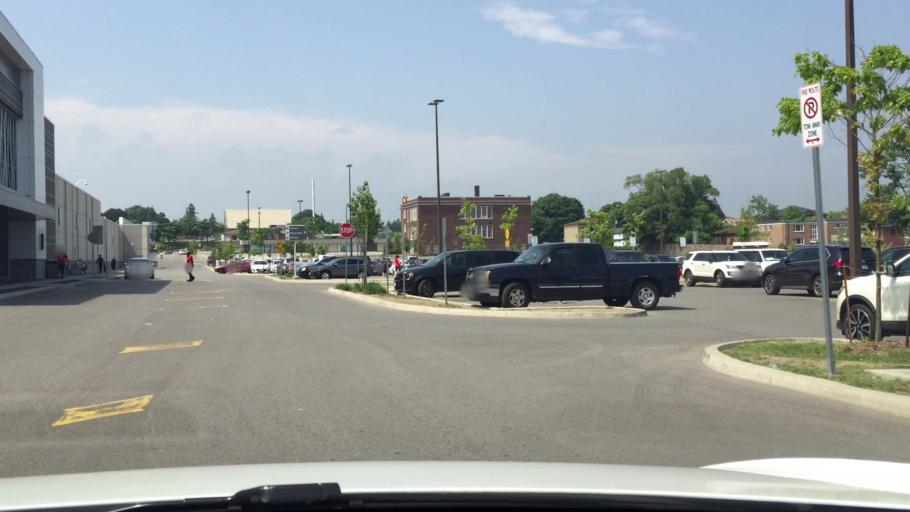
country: CA
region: Ontario
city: Oshawa
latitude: 43.8904
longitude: -78.8782
